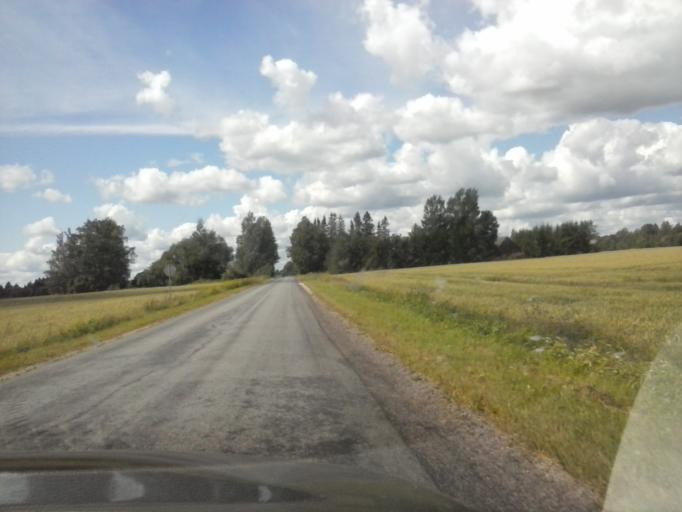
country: EE
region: Laeaene-Virumaa
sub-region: Rakke vald
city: Rakke
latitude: 59.0510
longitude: 26.3686
